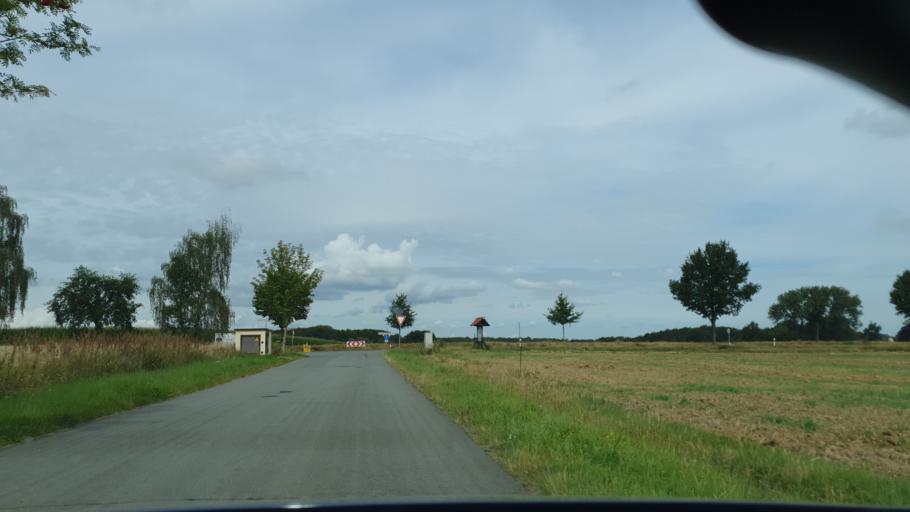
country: DE
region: North Rhine-Westphalia
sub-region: Regierungsbezirk Detmold
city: Werther
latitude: 52.1009
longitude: 8.4007
